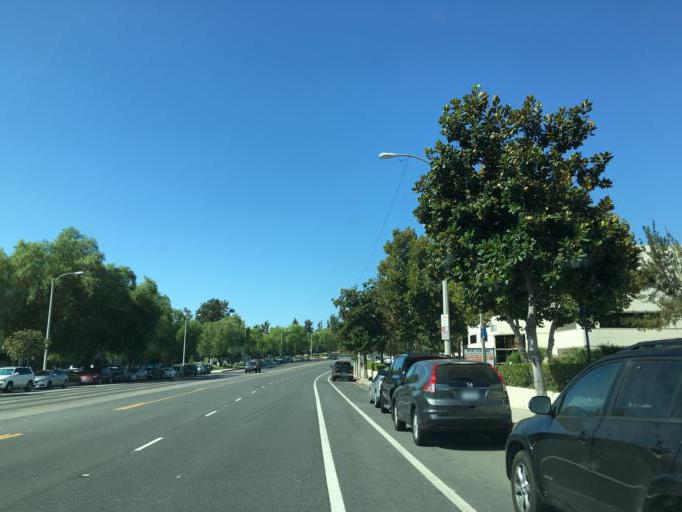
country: US
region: California
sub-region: Los Angeles County
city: Agoura
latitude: 34.1424
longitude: -118.7028
